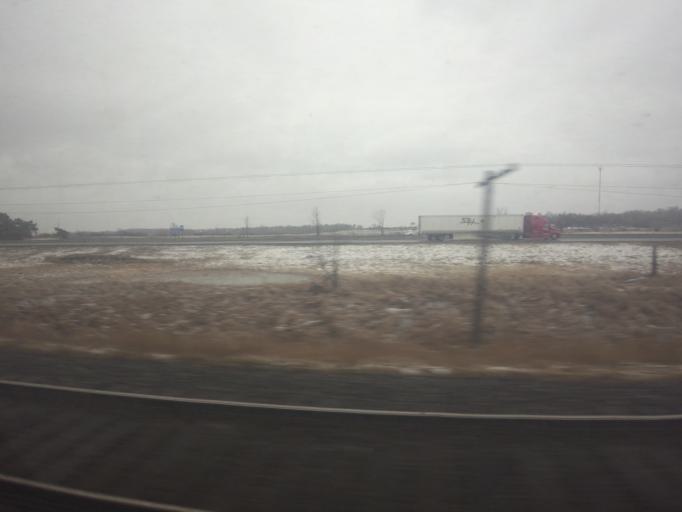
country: CA
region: Ontario
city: Kingston
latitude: 44.3206
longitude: -76.3566
